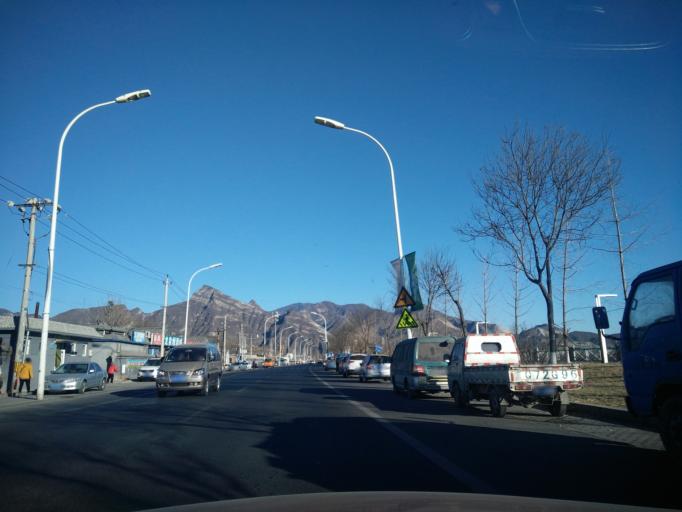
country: CN
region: Beijing
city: Junzhuang
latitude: 39.9816
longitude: 116.0822
